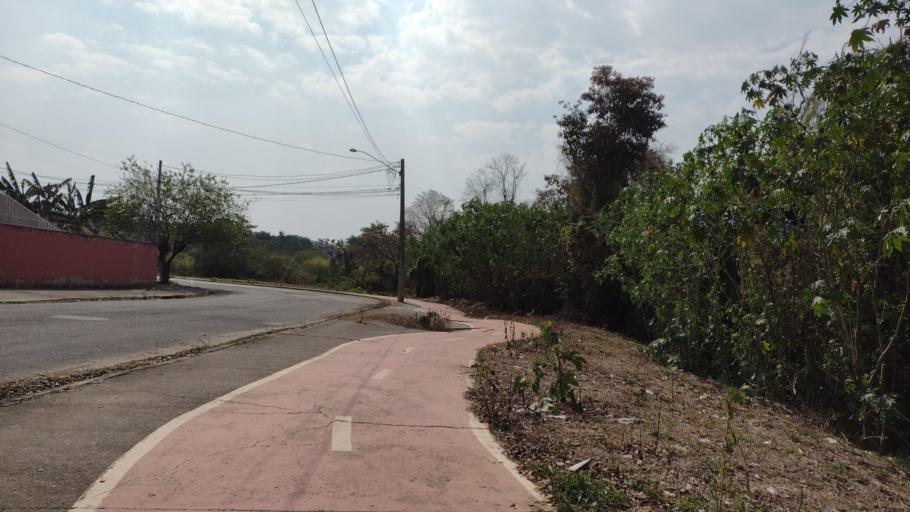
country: BR
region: Sao Paulo
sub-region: Sorocaba
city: Sorocaba
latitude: -23.4371
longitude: -47.4598
